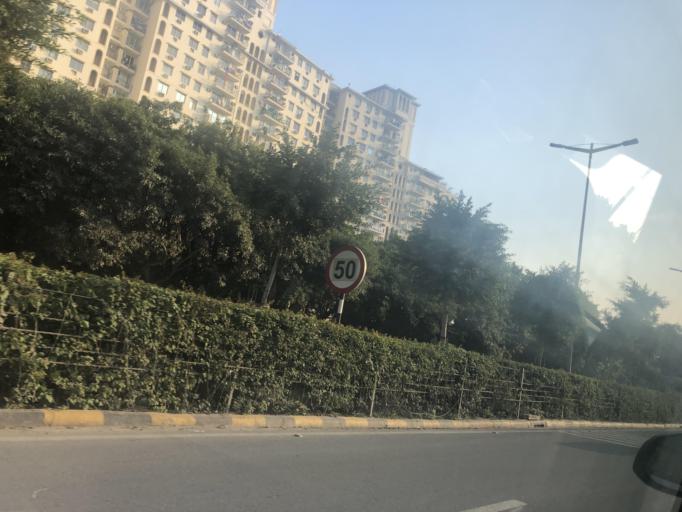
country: IN
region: Haryana
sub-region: Gurgaon
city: Gurgaon
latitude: 28.4910
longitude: 77.0908
